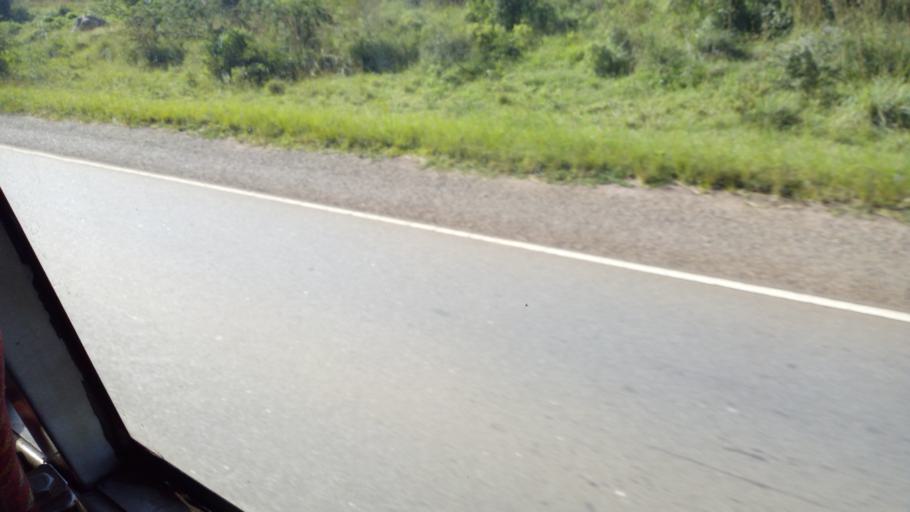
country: UG
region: Central Region
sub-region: Lyantonde District
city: Lyantonde
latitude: -0.4526
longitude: 31.0554
